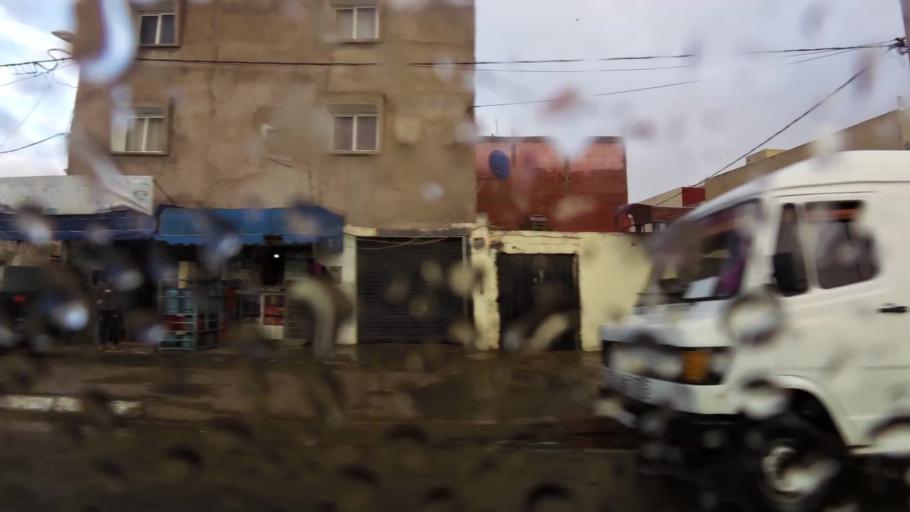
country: MA
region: Doukkala-Abda
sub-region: El-Jadida
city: El Jadida
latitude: 33.2398
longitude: -8.5165
